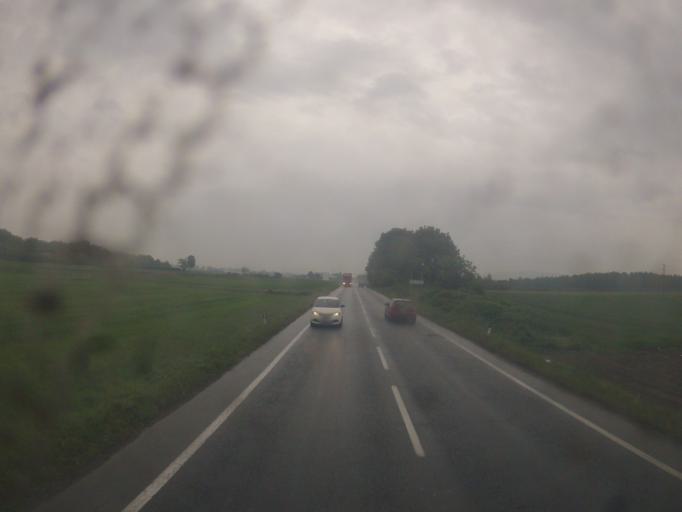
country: IT
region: Piedmont
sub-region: Provincia di Torino
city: Carignano
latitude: 44.9249
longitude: 7.6731
